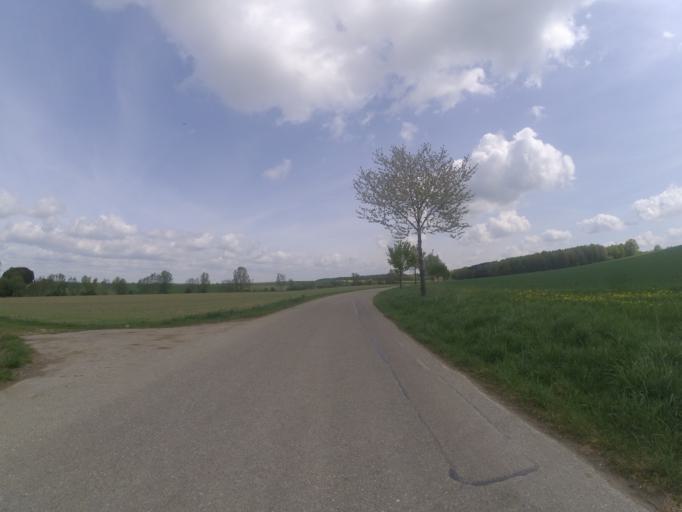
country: DE
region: Baden-Wuerttemberg
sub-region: Tuebingen Region
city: Griesingen
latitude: 48.2475
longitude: 9.7728
